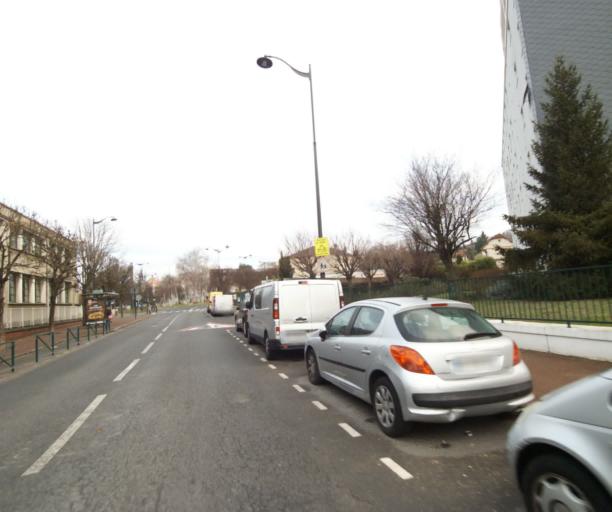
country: FR
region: Ile-de-France
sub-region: Departement des Hauts-de-Seine
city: Rueil-Malmaison
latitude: 48.8704
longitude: 2.2034
